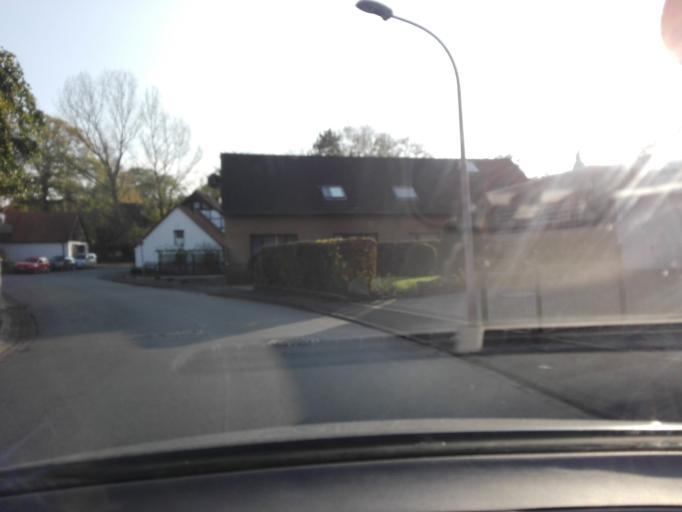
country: DE
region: North Rhine-Westphalia
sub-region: Regierungsbezirk Arnsberg
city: Unna
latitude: 51.5429
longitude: 7.7388
